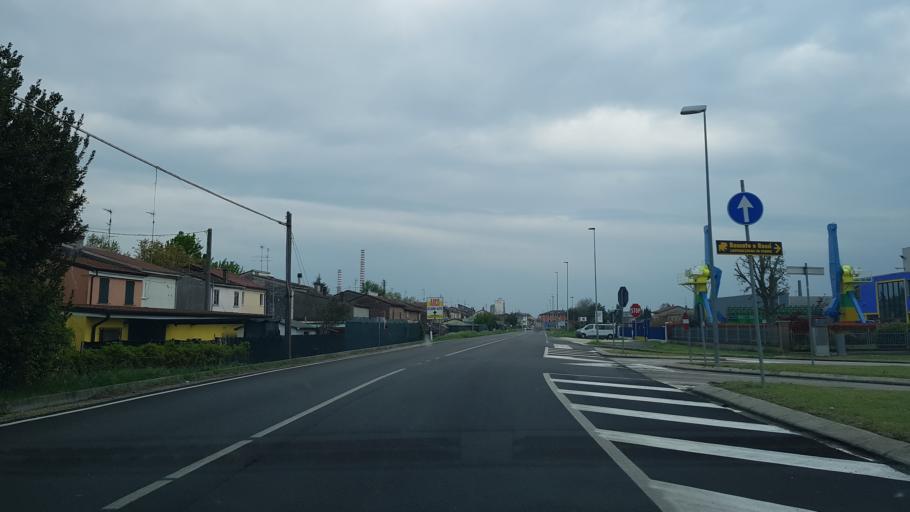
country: IT
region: Lombardy
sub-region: Provincia di Mantova
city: Ostiglia
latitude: 45.0763
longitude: 11.1355
